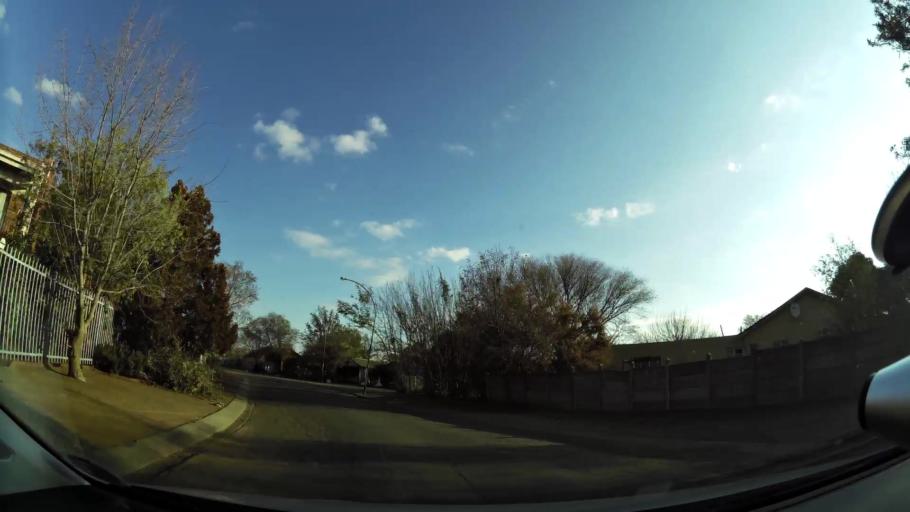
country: ZA
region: Orange Free State
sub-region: Mangaung Metropolitan Municipality
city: Bloemfontein
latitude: -29.1620
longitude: 26.1812
